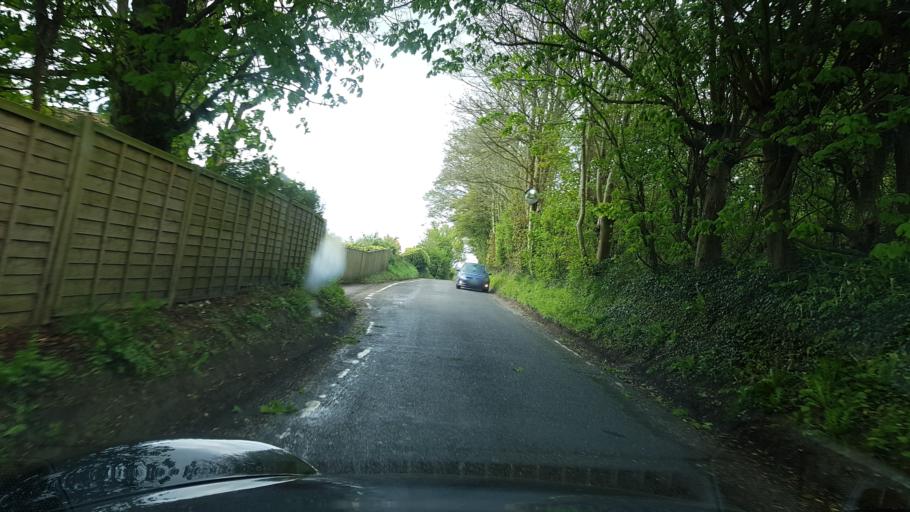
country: GB
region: England
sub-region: Hampshire
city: Kingsclere
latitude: 51.3231
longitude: -1.2524
